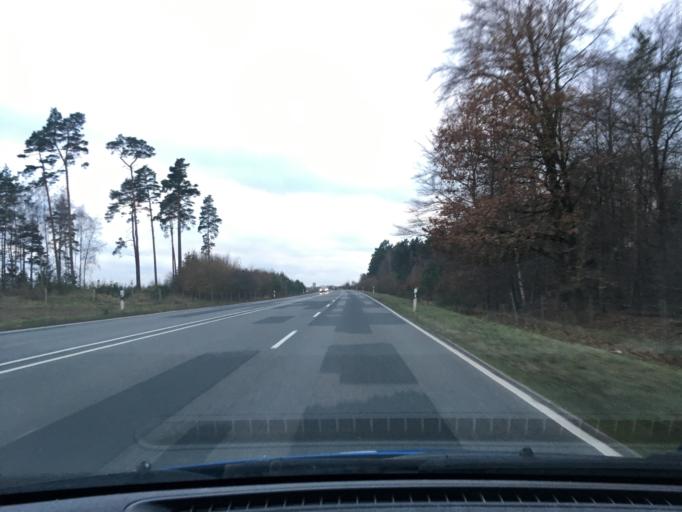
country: DE
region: Lower Saxony
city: Uelzen
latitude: 52.9325
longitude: 10.5532
